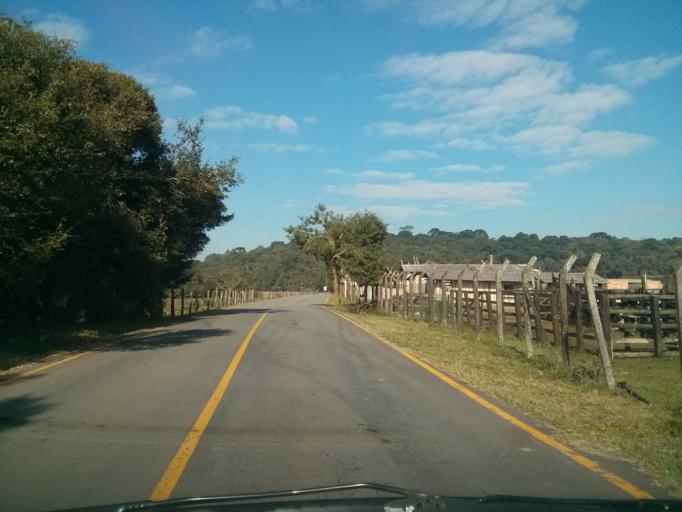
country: BR
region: Parana
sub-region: Sao Jose Dos Pinhais
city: Sao Jose dos Pinhais
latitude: -25.5512
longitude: -49.2255
